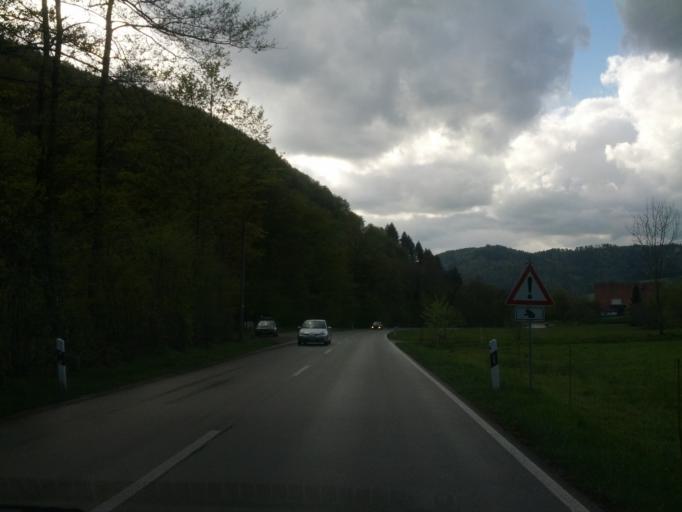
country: DE
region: Baden-Wuerttemberg
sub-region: Freiburg Region
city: Glottertal
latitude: 48.0404
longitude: 7.9842
